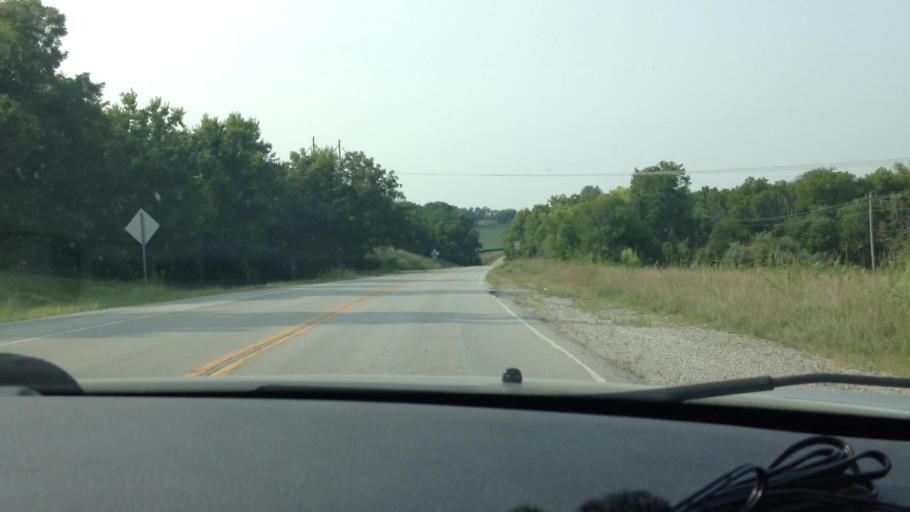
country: US
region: Missouri
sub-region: Platte County
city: Platte City
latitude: 39.3870
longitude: -94.7936
